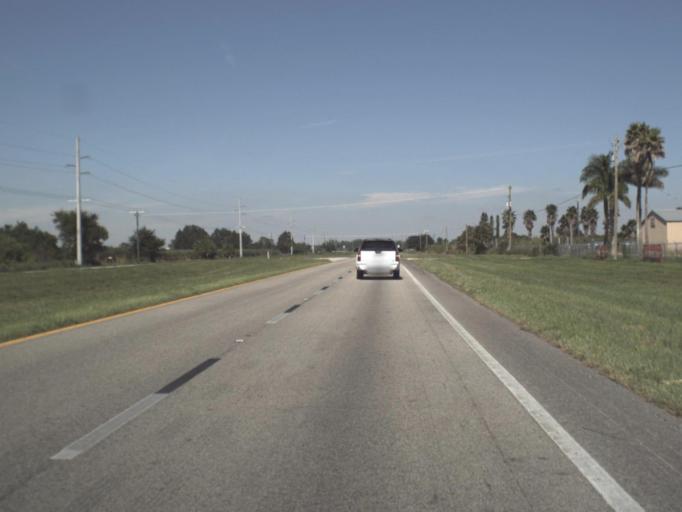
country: US
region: Florida
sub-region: Glades County
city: Moore Haven
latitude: 26.8158
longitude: -81.0824
